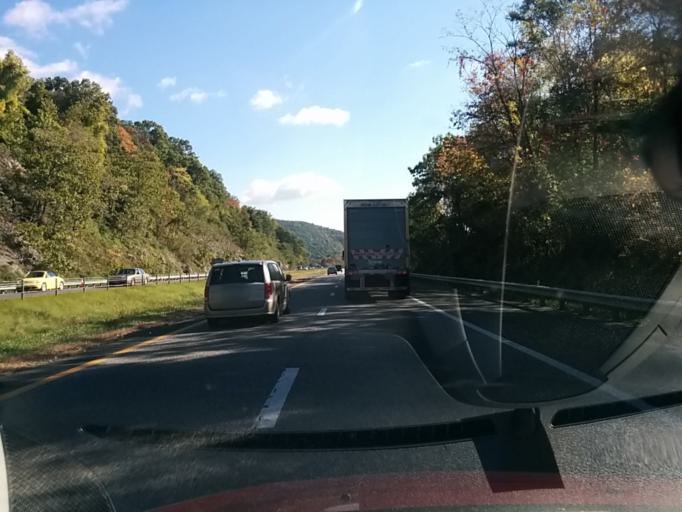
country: US
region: Virginia
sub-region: City of Waynesboro
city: Waynesboro
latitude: 38.0389
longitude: -78.8361
